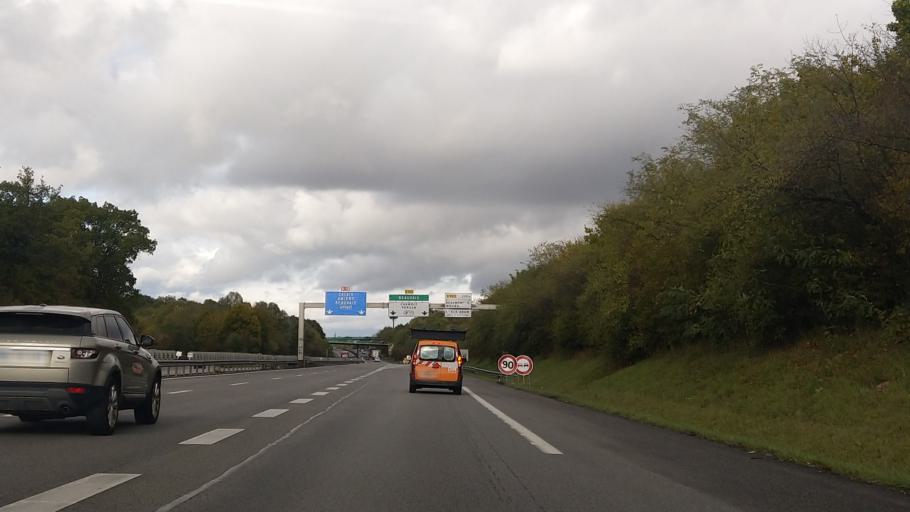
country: FR
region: Ile-de-France
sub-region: Departement du Val-d'Oise
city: Mours
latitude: 49.1211
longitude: 2.2527
